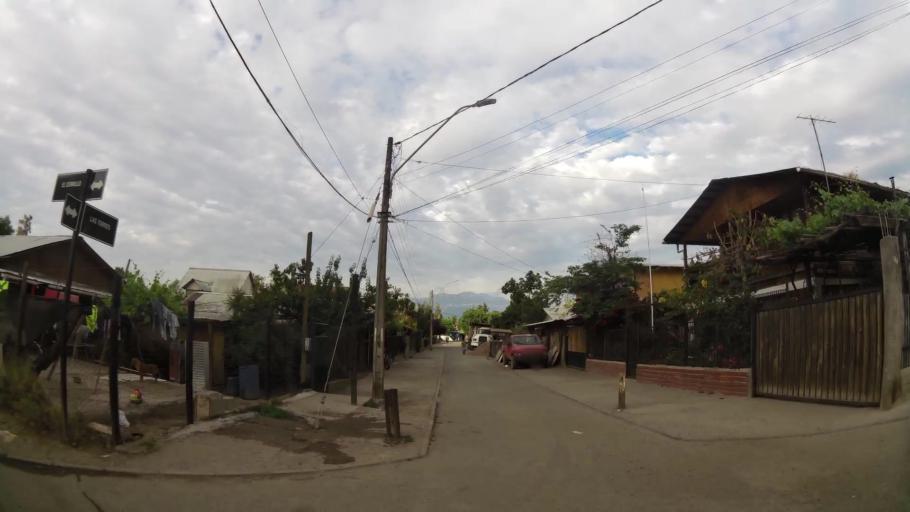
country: CL
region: Santiago Metropolitan
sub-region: Provincia de Maipo
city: San Bernardo
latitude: -33.6477
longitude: -70.6661
